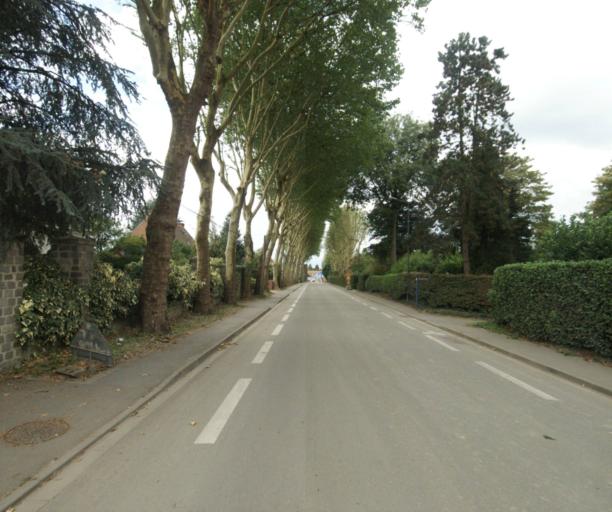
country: FR
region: Nord-Pas-de-Calais
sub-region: Departement du Nord
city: Villeneuve-d'Ascq
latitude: 50.6252
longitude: 3.1571
